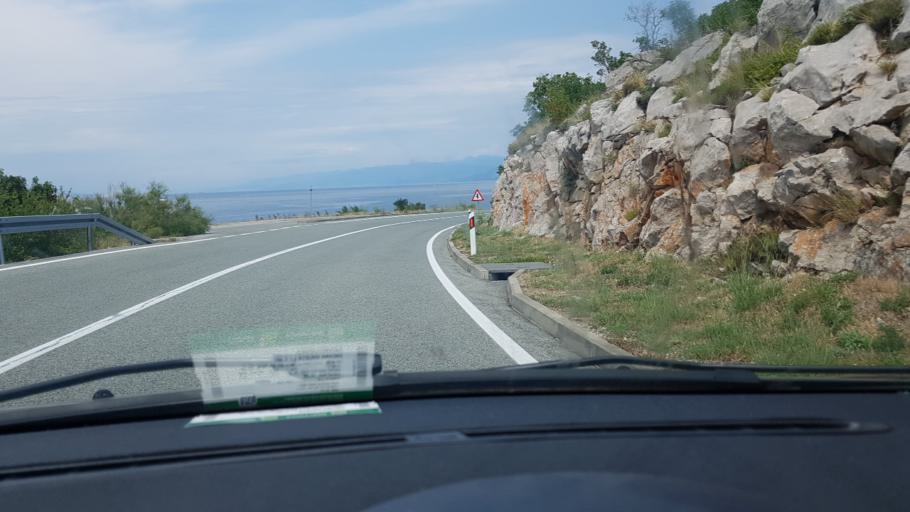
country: HR
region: Licko-Senjska
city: Senj
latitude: 44.9137
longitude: 14.9136
